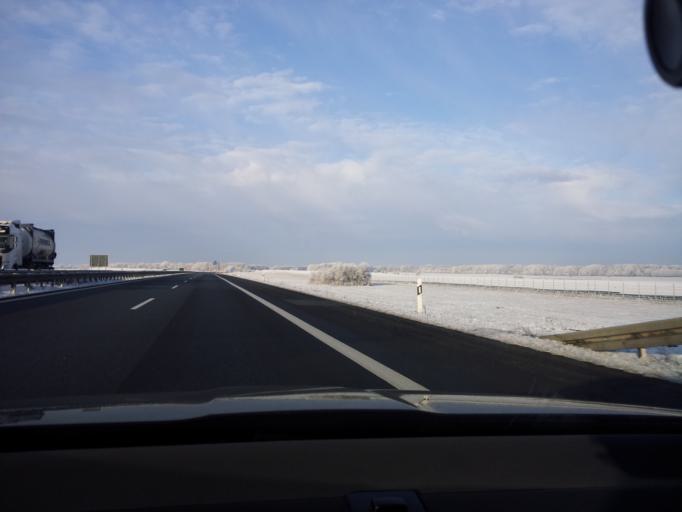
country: DE
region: Brandenburg
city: Triglitz
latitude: 53.2717
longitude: 12.1104
